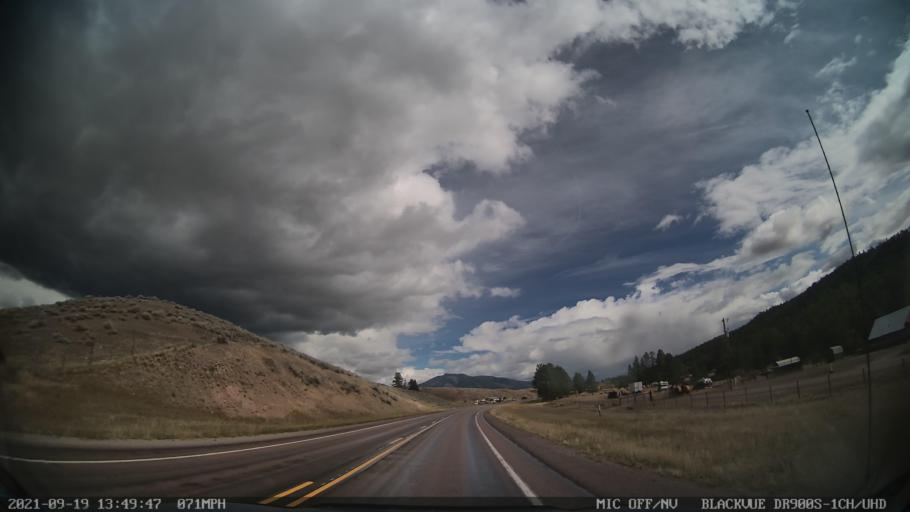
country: US
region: Montana
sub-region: Missoula County
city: Seeley Lake
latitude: 47.0435
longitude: -113.2140
